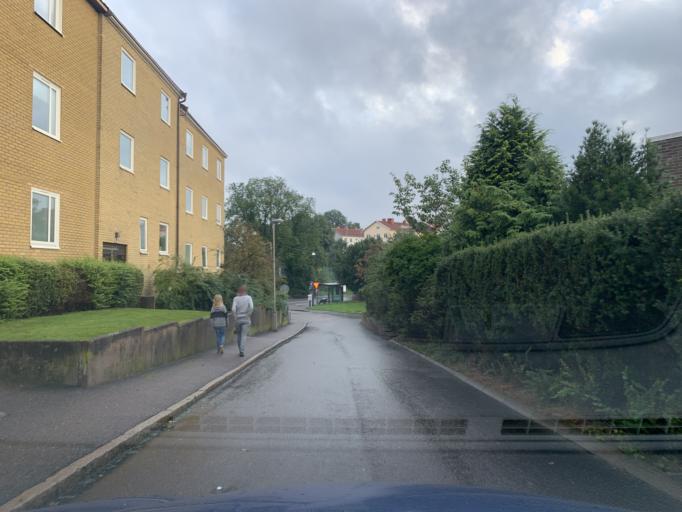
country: SE
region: Vaestra Goetaland
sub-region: Goteborg
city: Goeteborg
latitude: 57.7095
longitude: 12.0014
